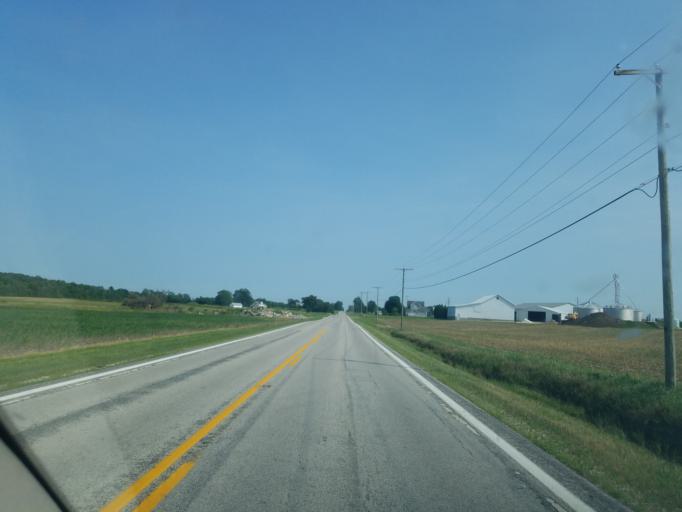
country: US
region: Ohio
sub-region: Wyandot County
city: Carey
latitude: 41.0405
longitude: -83.3085
